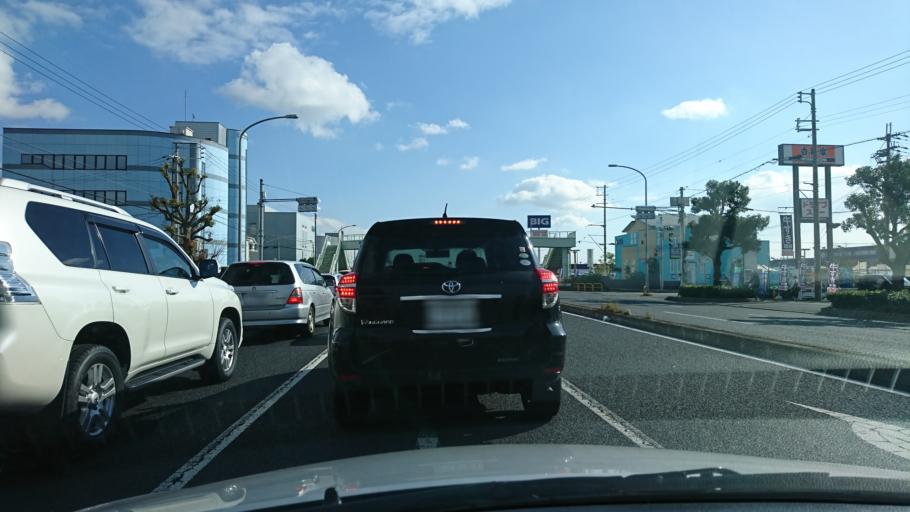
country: JP
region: Hyogo
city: Kakogawacho-honmachi
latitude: 34.7586
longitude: 134.8200
